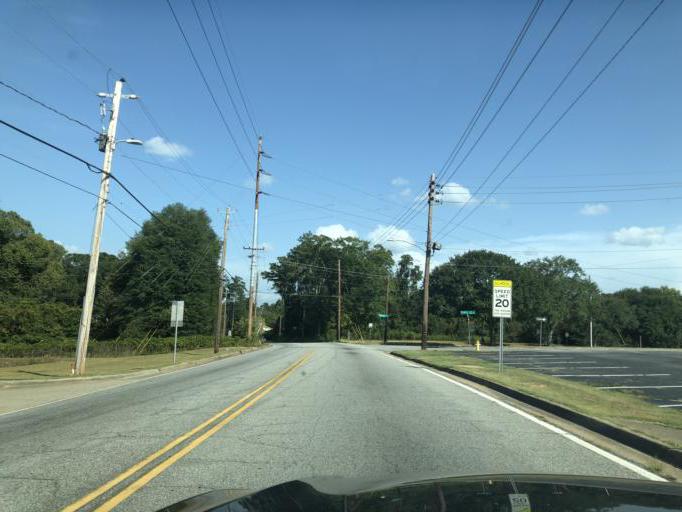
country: US
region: Georgia
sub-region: Muscogee County
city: Columbus
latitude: 32.4847
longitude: -84.9339
